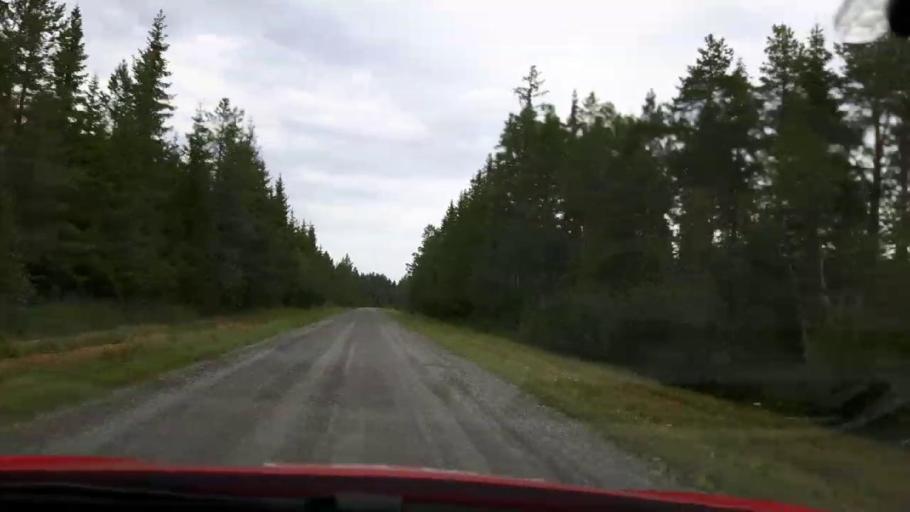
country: SE
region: Jaemtland
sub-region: Stroemsunds Kommun
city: Stroemsund
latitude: 63.7367
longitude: 15.5591
